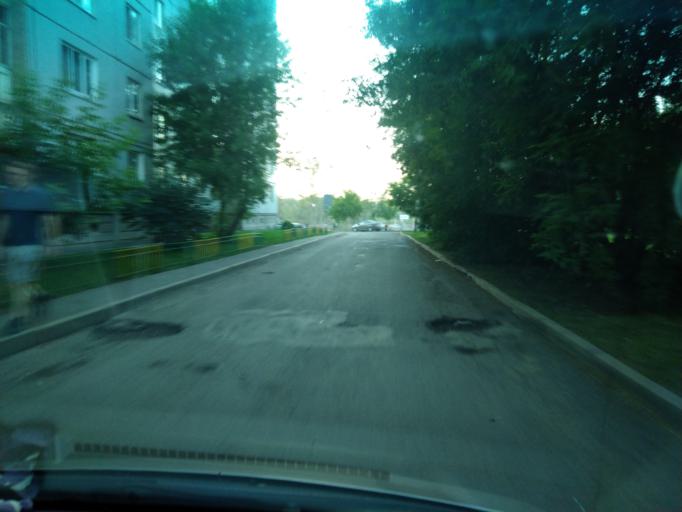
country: RU
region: Krasnoyarskiy
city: Krasnoyarsk
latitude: 55.9868
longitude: 92.8702
